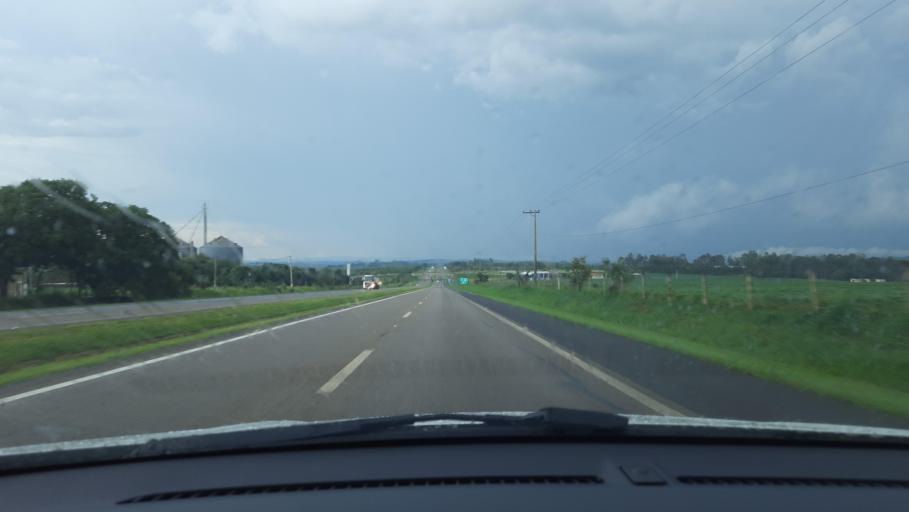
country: BR
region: Sao Paulo
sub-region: Casa Branca
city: Casa Branca
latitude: -21.7555
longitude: -47.0709
